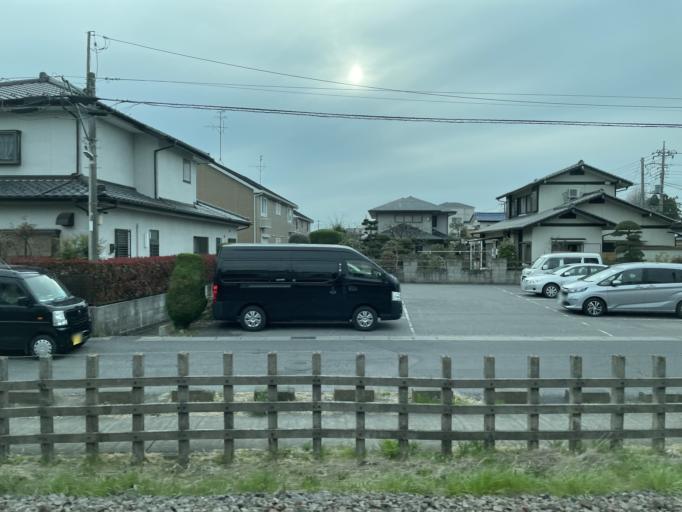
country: JP
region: Saitama
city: Kasukabe
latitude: 35.9702
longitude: 139.7643
